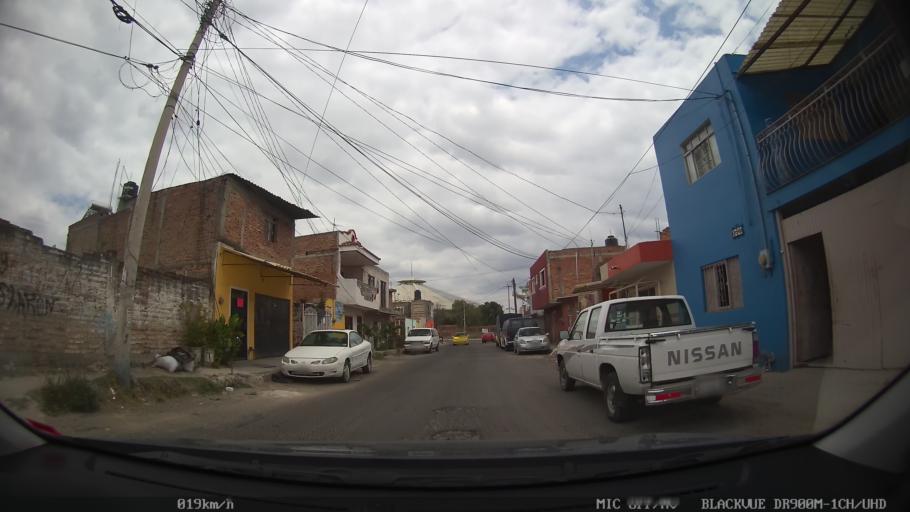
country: MX
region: Jalisco
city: Tlaquepaque
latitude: 20.6544
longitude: -103.2670
